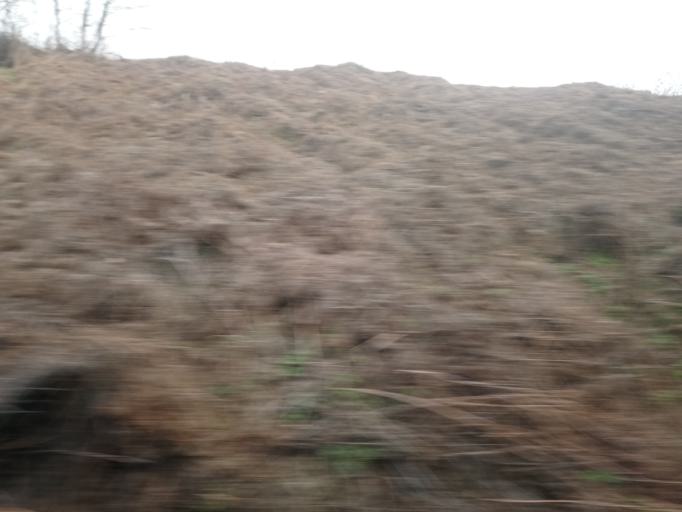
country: GB
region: England
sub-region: Suffolk
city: Ipswich
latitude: 52.0284
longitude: 1.1367
